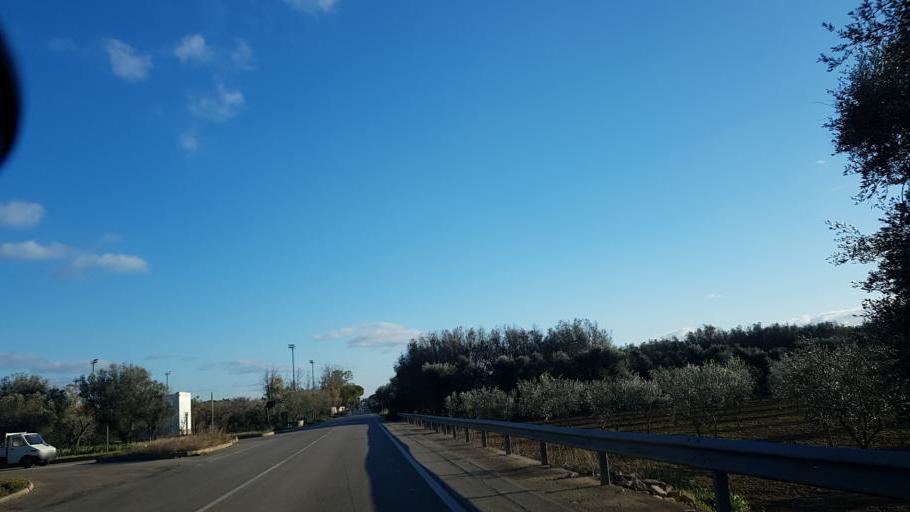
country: IT
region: Apulia
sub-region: Provincia di Lecce
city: Squinzano
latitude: 40.4470
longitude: 18.0313
